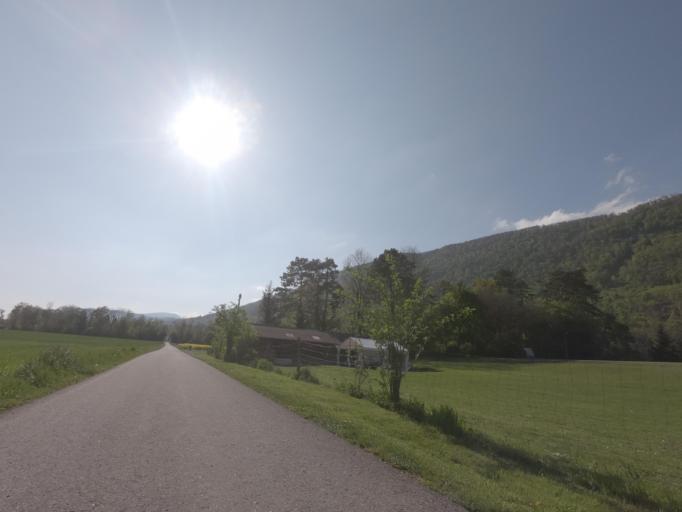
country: CH
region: Bern
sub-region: Biel/Bienne District
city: Pieterlen
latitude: 47.1681
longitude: 7.3130
